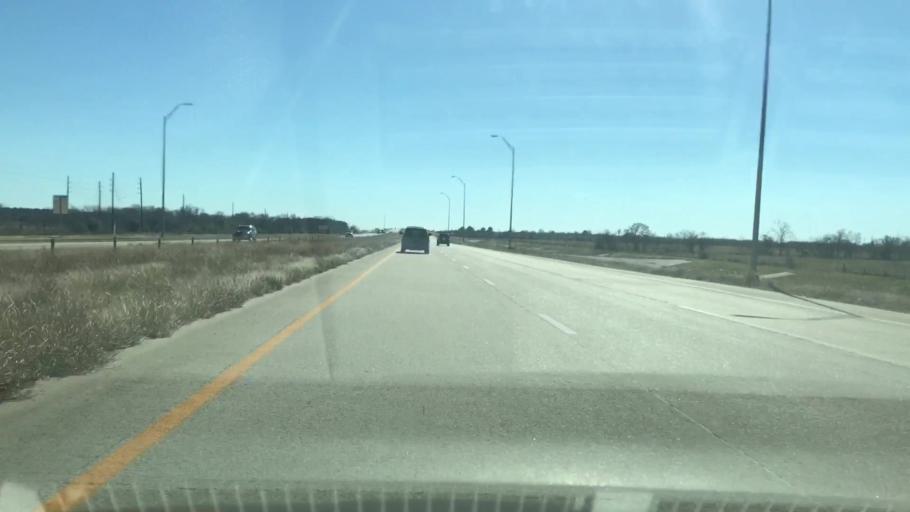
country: US
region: Texas
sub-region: Harris County
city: Cypress
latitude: 29.8990
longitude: -95.7584
